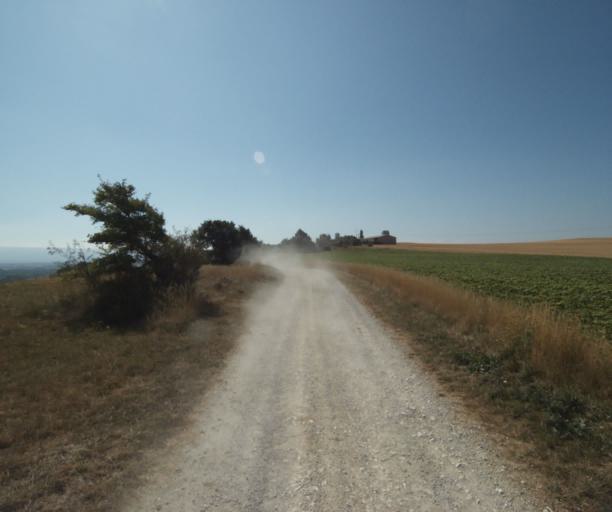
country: FR
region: Midi-Pyrenees
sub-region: Departement de la Haute-Garonne
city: Saint-Felix-Lauragais
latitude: 43.5073
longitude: 1.9321
